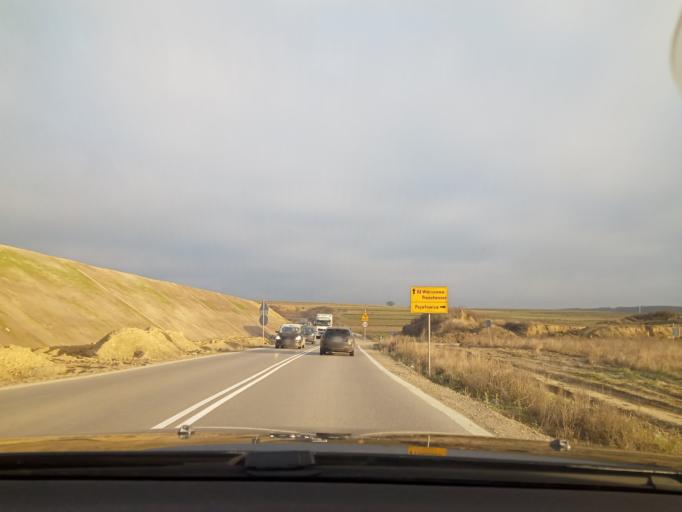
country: PL
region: Lesser Poland Voivodeship
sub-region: Powiat miechowski
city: Miechow
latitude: 50.3159
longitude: 20.0387
